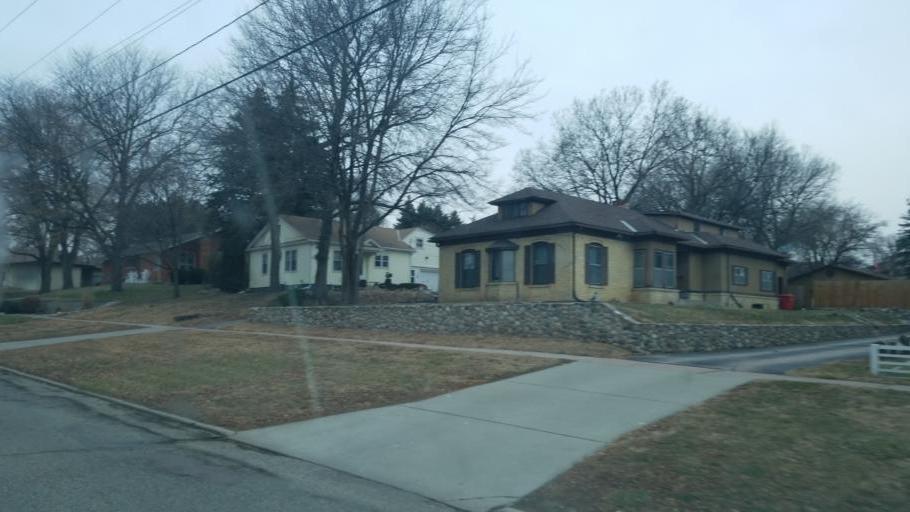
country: US
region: South Dakota
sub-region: Yankton County
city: Yankton
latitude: 42.8762
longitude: -97.4017
